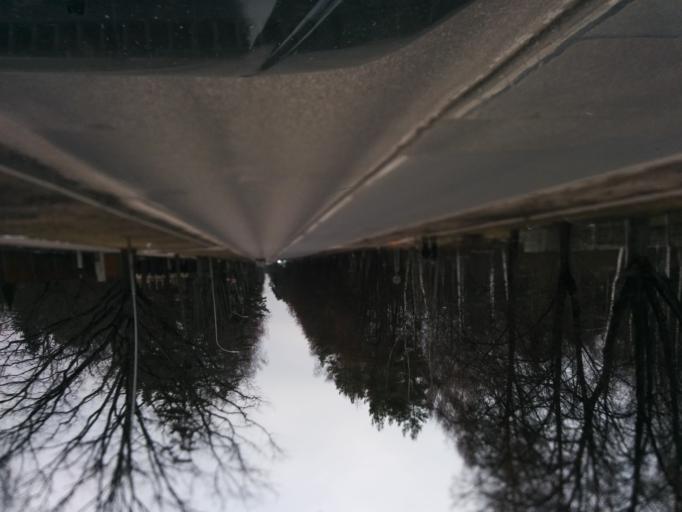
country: LV
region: Jurmala
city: Jurmala
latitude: 56.9603
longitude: 23.7058
